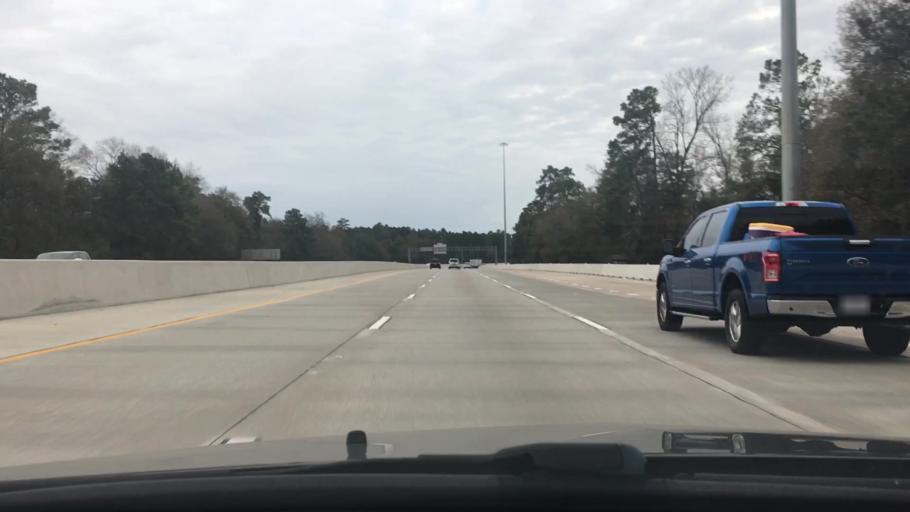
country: US
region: Texas
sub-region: Harris County
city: Spring
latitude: 30.0828
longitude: -95.4116
